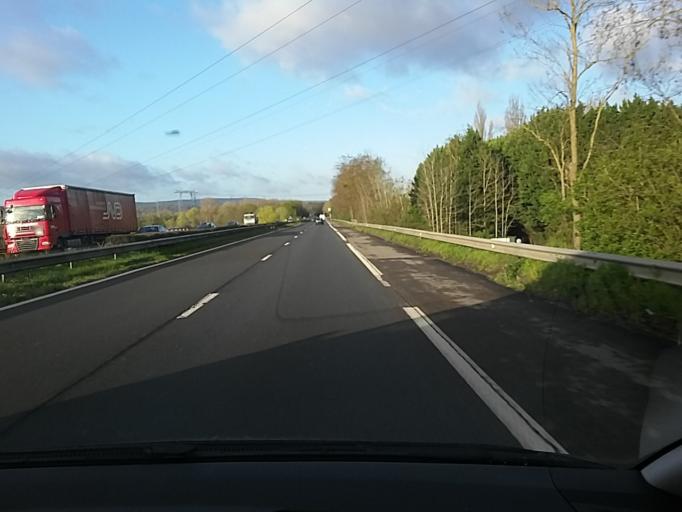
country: FR
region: Picardie
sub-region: Departement de l'Oise
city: Verberie
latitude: 49.3334
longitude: 2.7231
